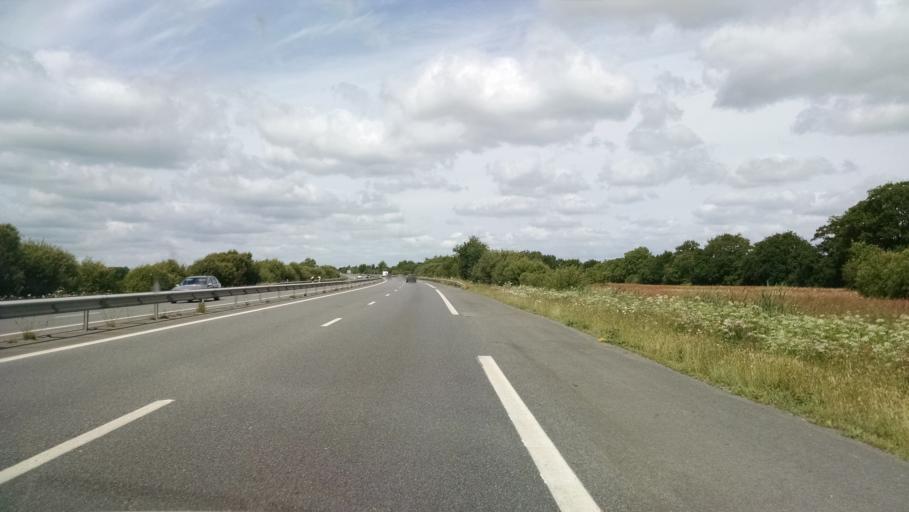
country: FR
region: Pays de la Loire
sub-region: Departement de la Loire-Atlantique
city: Sainte-Anne-sur-Brivet
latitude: 47.4156
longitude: -2.0295
